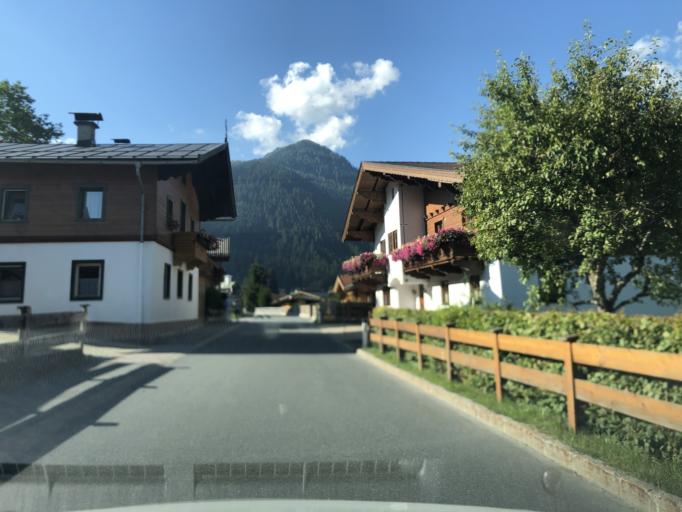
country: AT
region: Tyrol
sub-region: Politischer Bezirk Kitzbuhel
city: Kirchberg in Tirol
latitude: 47.3839
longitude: 12.3071
